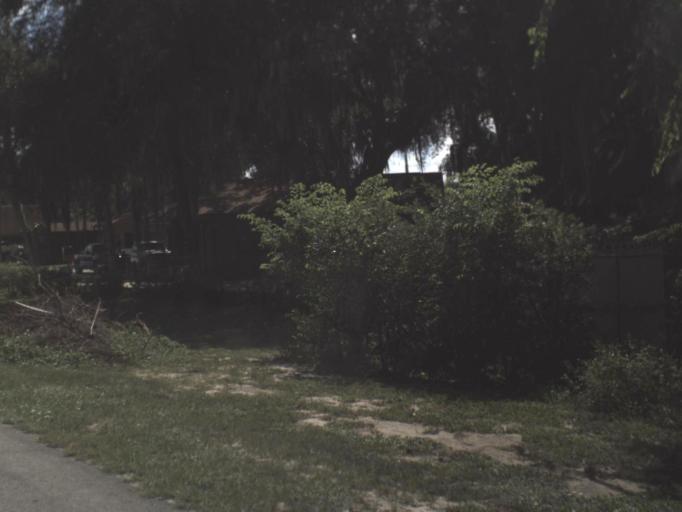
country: US
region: Florida
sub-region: Okeechobee County
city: Taylor Creek
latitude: 27.1849
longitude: -80.7399
